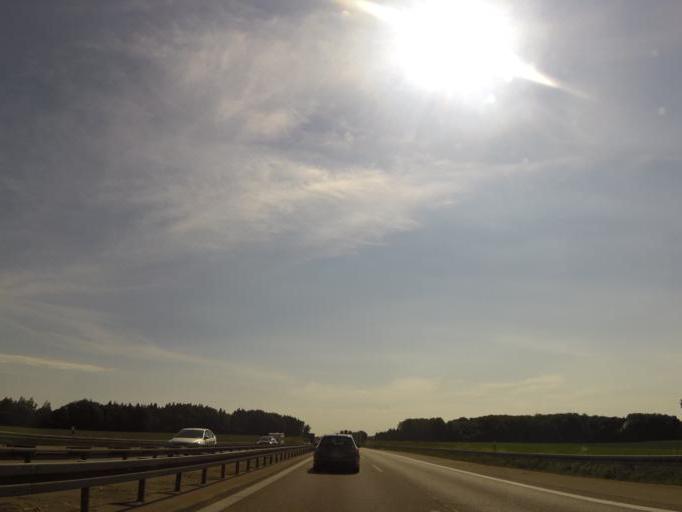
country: DE
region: Baden-Wuerttemberg
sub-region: Tuebingen Region
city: Merklingen
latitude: 48.5181
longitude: 9.7673
